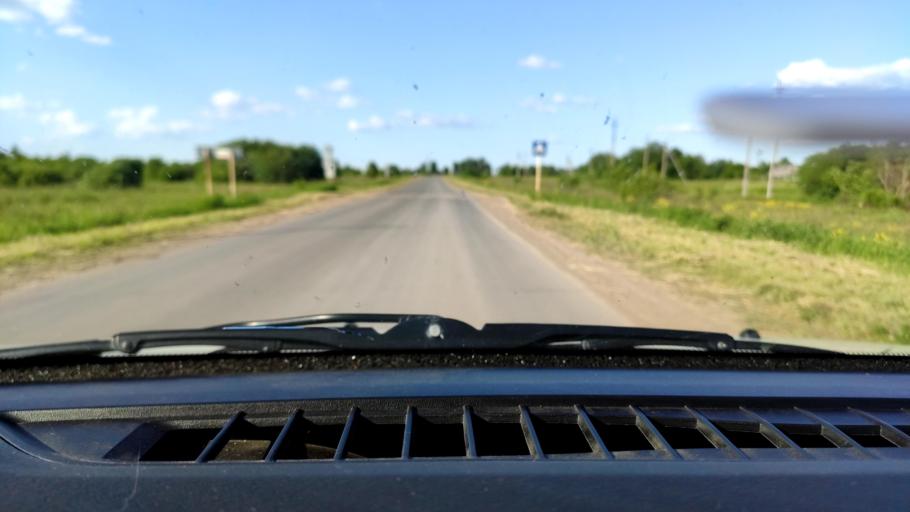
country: RU
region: Perm
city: Uinskoye
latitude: 57.0951
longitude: 56.6412
